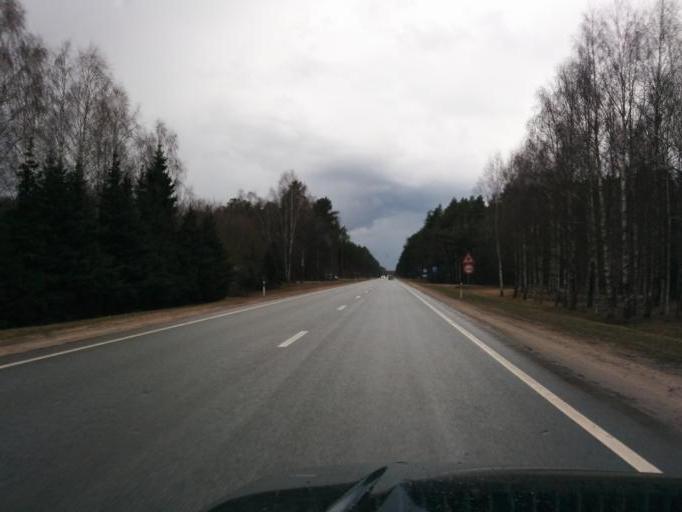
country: LV
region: Babite
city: Pinki
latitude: 56.8841
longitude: 23.9455
